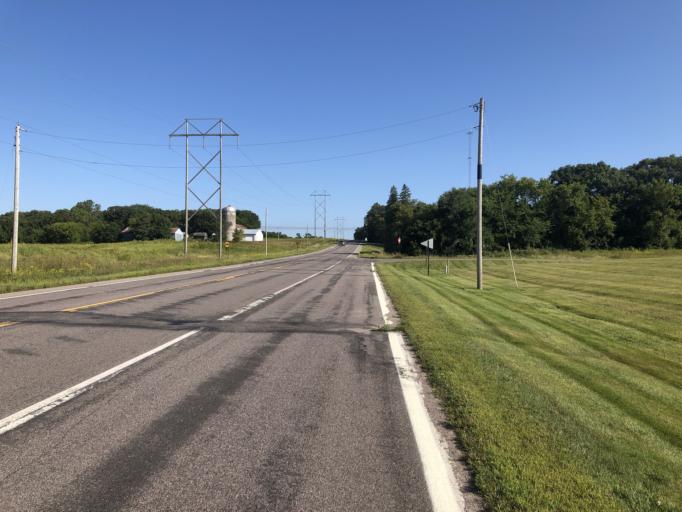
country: US
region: Minnesota
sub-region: Sherburne County
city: Becker
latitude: 45.4251
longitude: -93.8400
